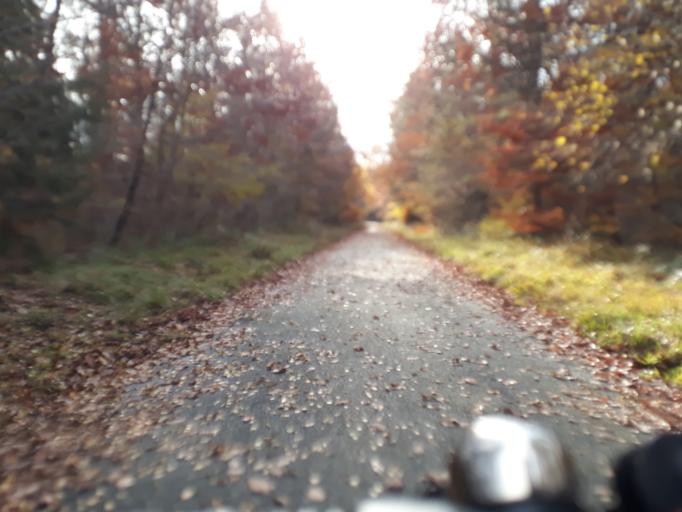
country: FR
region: Ile-de-France
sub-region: Departement de Seine-et-Marne
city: Bois-le-Roi
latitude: 48.4623
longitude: 2.6850
